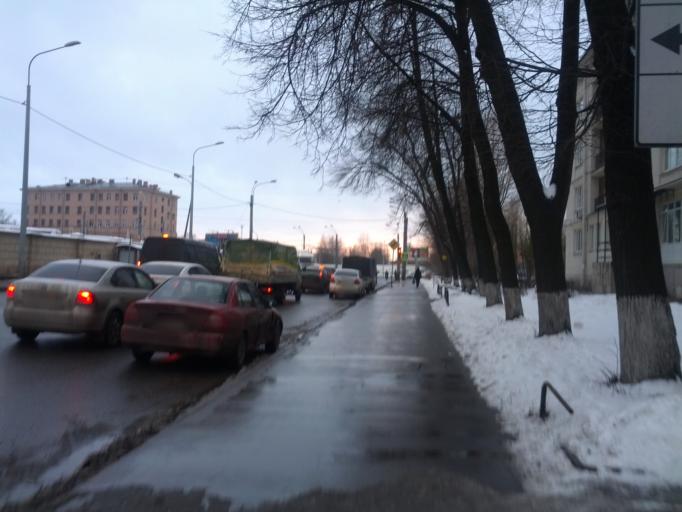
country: RU
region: St.-Petersburg
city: Centralniy
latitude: 59.9067
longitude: 30.3549
